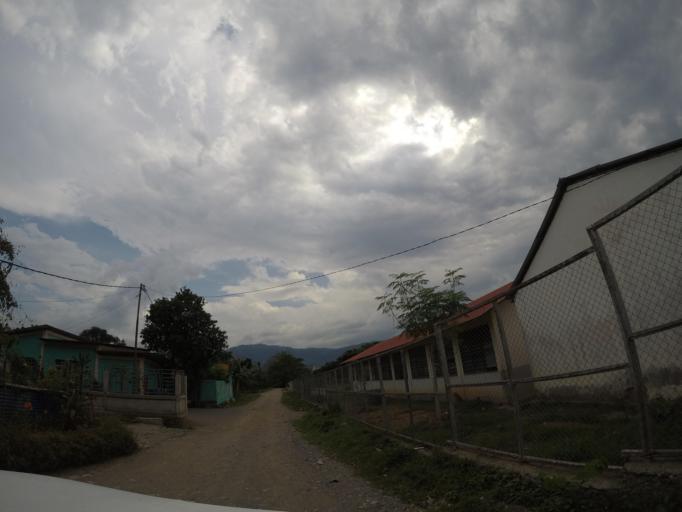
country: TL
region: Ermera
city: Gleno
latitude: -8.7120
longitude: 125.4423
